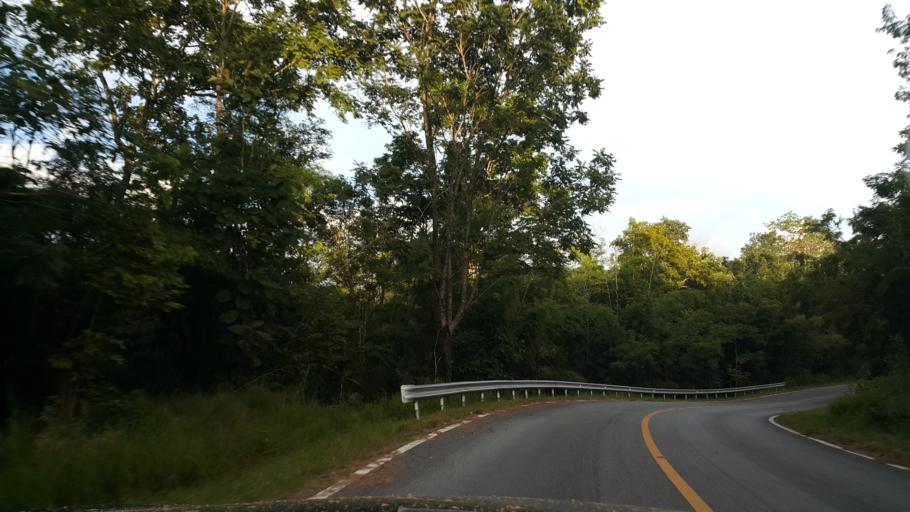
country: TH
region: Mae Hong Son
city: Mae Hi
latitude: 19.1801
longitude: 98.4039
